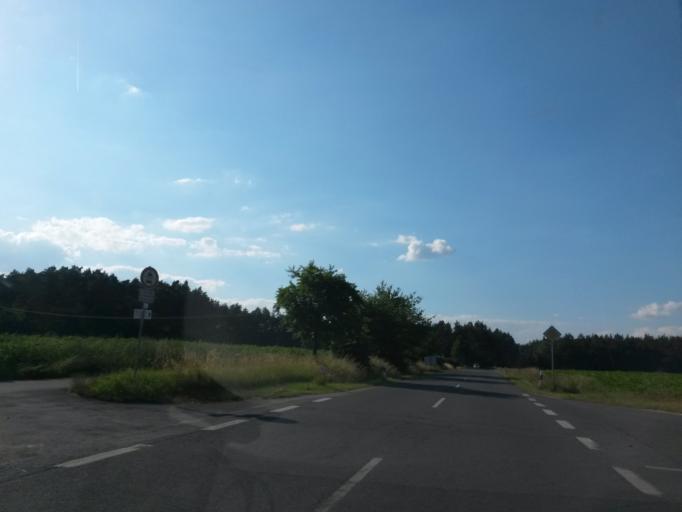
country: DE
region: Bavaria
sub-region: Regierungsbezirk Mittelfranken
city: Zirndorf
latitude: 49.4541
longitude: 10.9187
